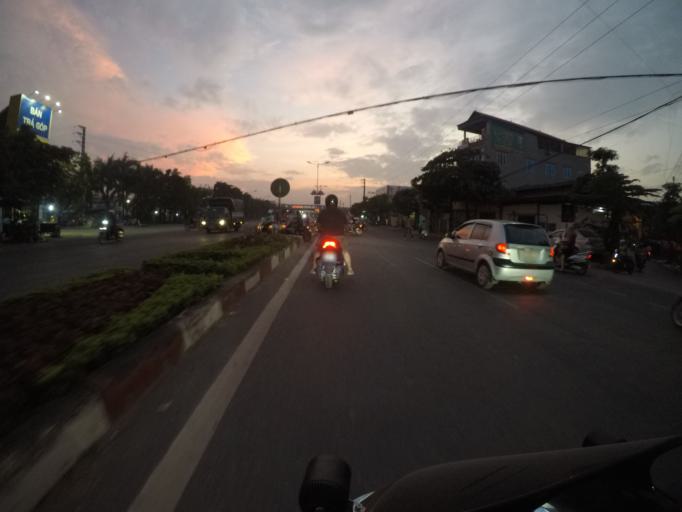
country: VN
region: Vinh Phuc
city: Phuc Yen
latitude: 21.2376
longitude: 105.7234
